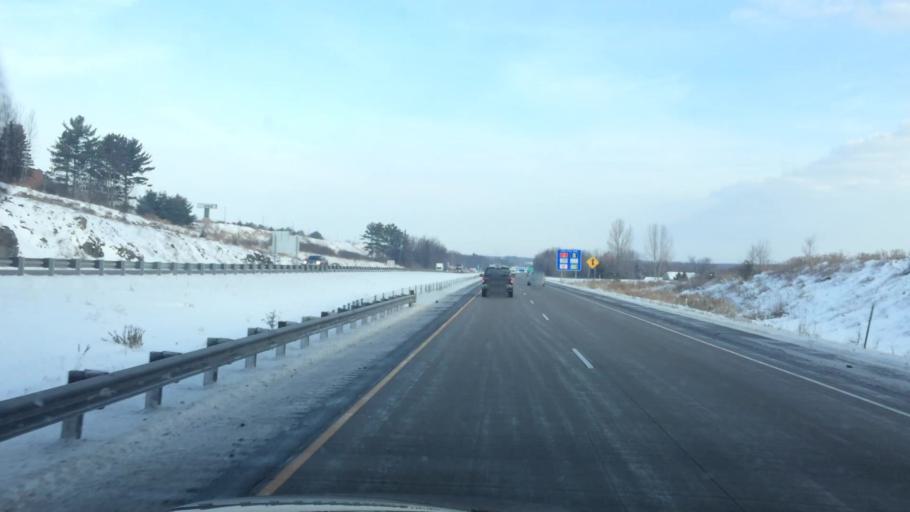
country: US
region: Wisconsin
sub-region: Marathon County
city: Wausau
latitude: 44.9698
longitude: -89.6561
